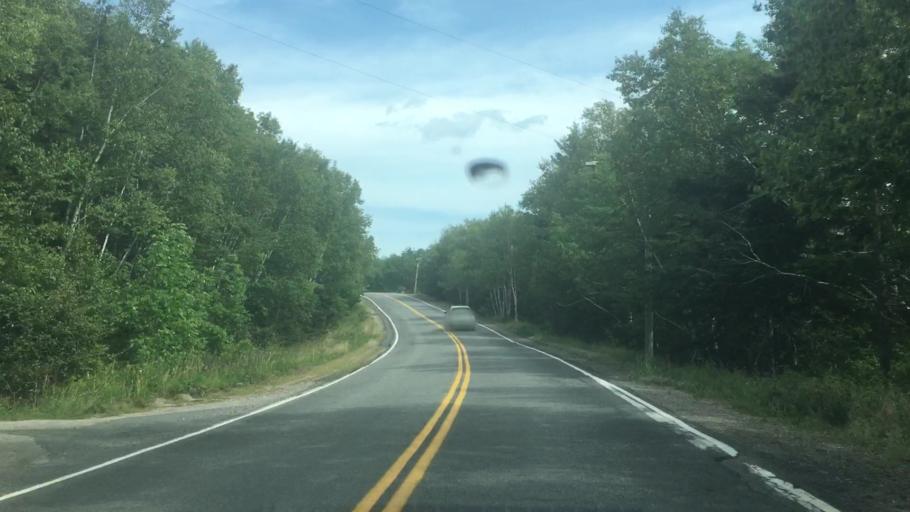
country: CA
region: Nova Scotia
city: Sydney Mines
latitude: 46.6354
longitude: -60.4173
